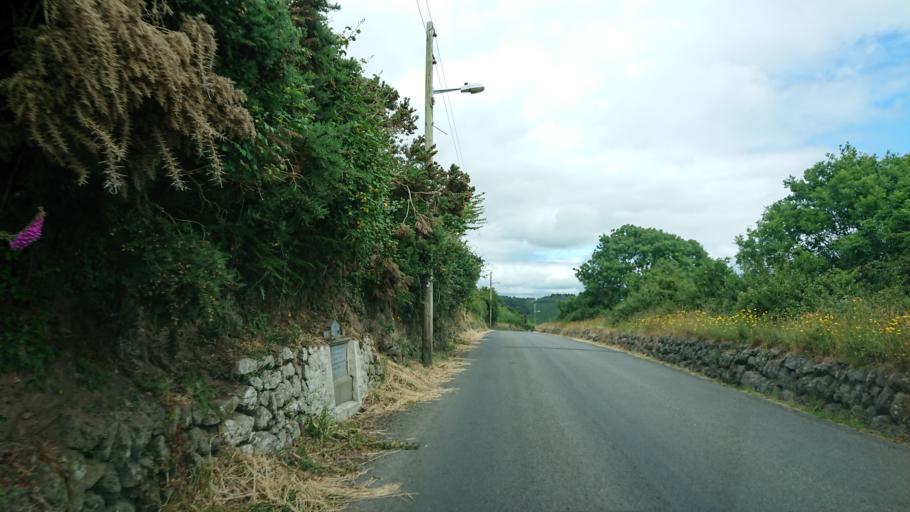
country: IE
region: Munster
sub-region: Waterford
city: Dunmore East
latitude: 52.2343
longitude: -6.9721
